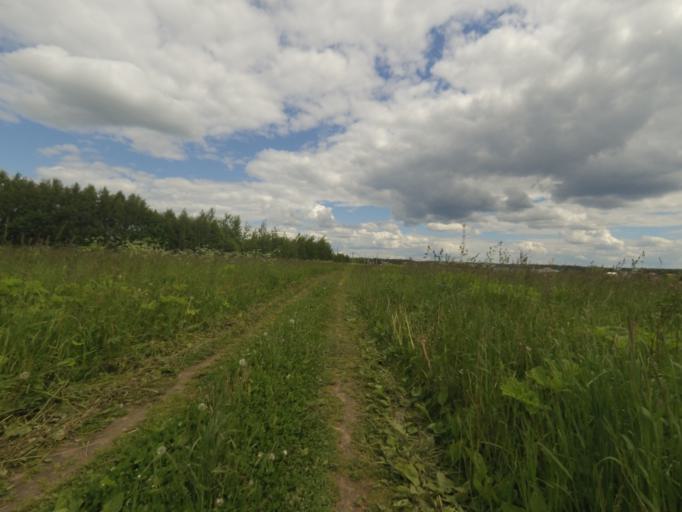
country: RU
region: Moskovskaya
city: Marfino
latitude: 56.0495
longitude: 37.5268
